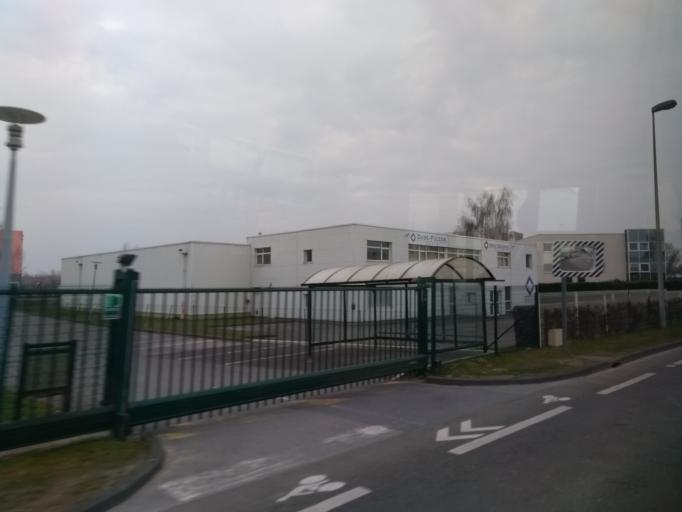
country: FR
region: Picardie
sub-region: Departement de l'Oise
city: Jaux
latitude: 49.3917
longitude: 2.7922
